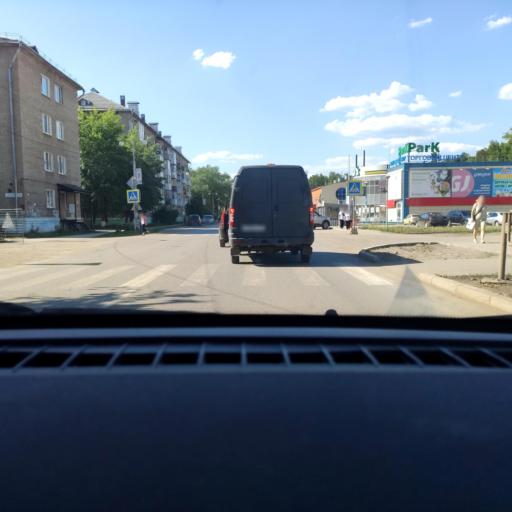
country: RU
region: Perm
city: Krasnokamsk
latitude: 58.0818
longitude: 55.7575
